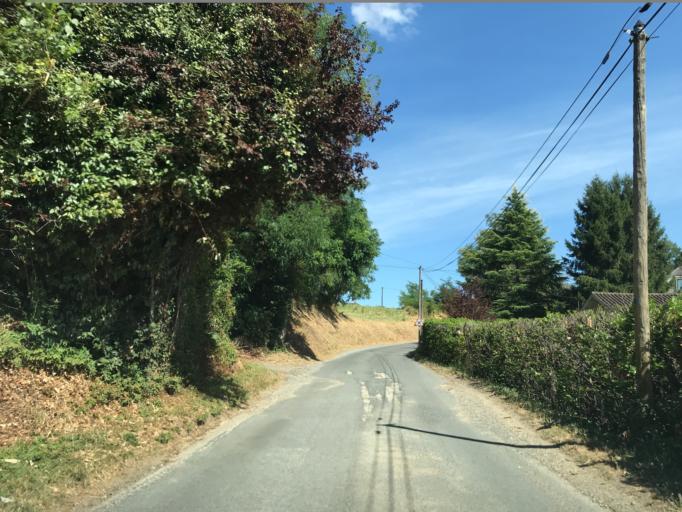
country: FR
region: Aquitaine
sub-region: Departement de la Dordogne
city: Sarlat-la-Caneda
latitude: 44.8920
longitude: 1.2037
